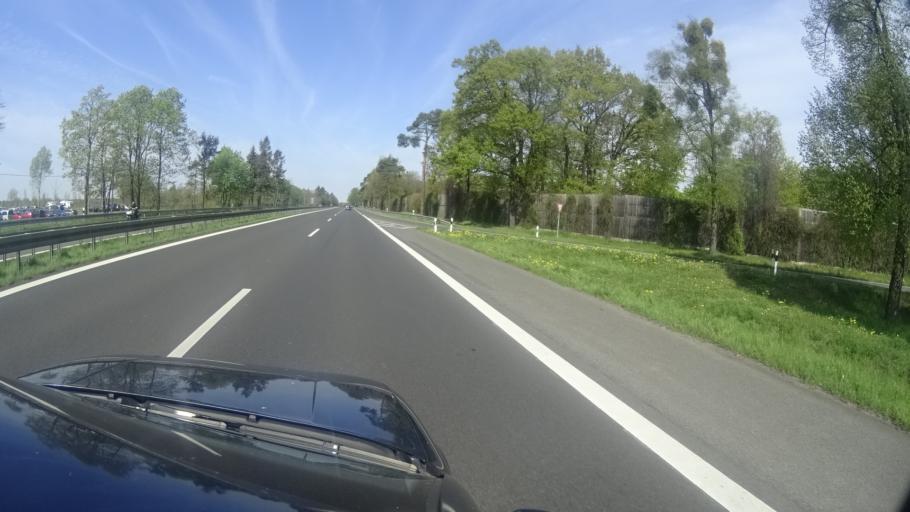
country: DE
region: Brandenburg
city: Brieselang
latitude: 52.5346
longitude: 12.9973
